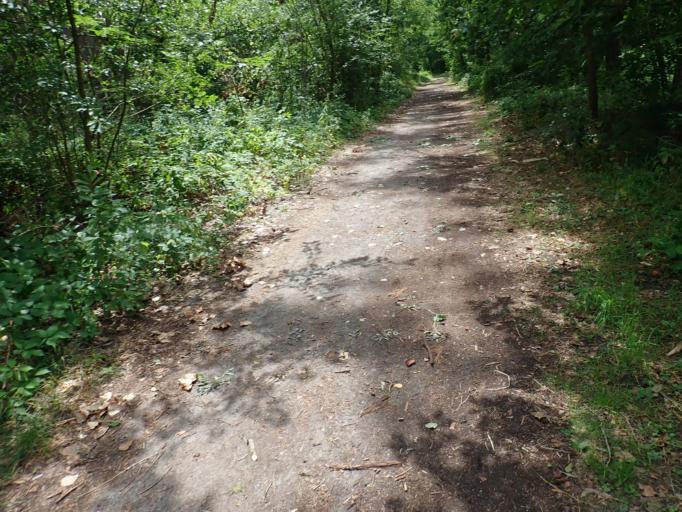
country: BE
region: Flanders
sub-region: Provincie Vlaams-Brabant
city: Keerbergen
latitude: 50.9982
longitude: 4.6196
